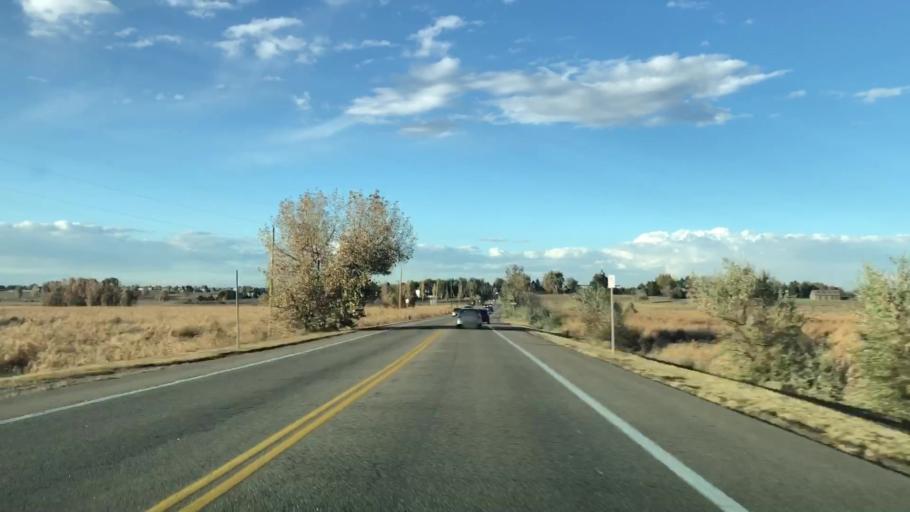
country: US
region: Colorado
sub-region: Larimer County
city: Loveland
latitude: 40.4846
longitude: -105.0393
